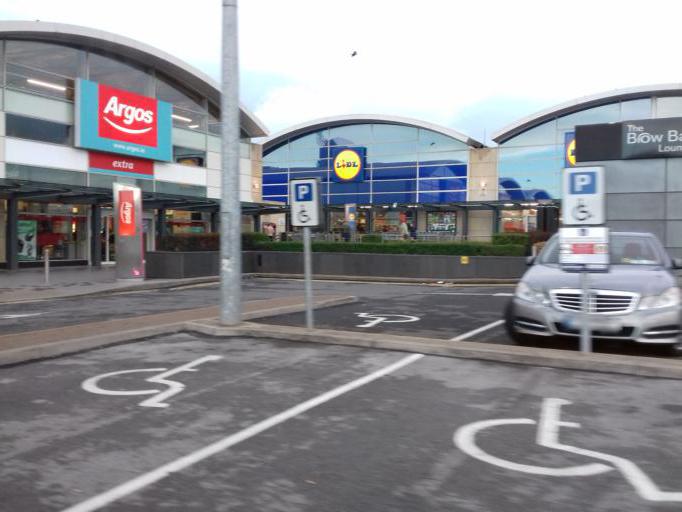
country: IE
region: Leinster
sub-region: Fingal County
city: Blanchardstown
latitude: 53.3912
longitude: -6.3860
